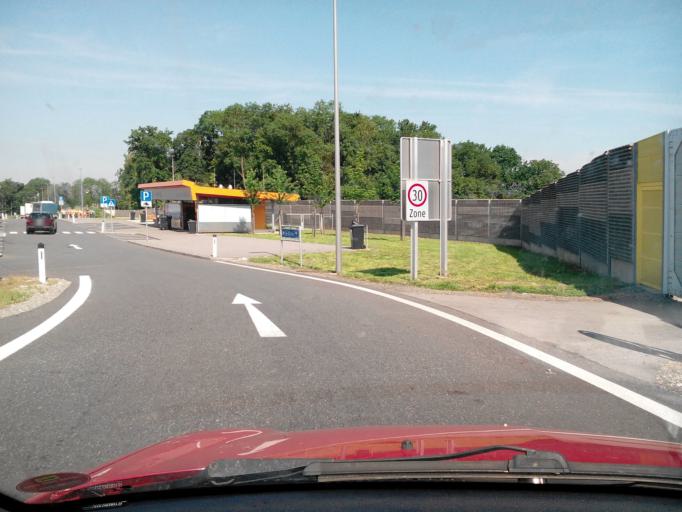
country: AT
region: Upper Austria
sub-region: Politischer Bezirk Linz-Land
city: Enns
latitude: 48.2063
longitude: 14.4544
